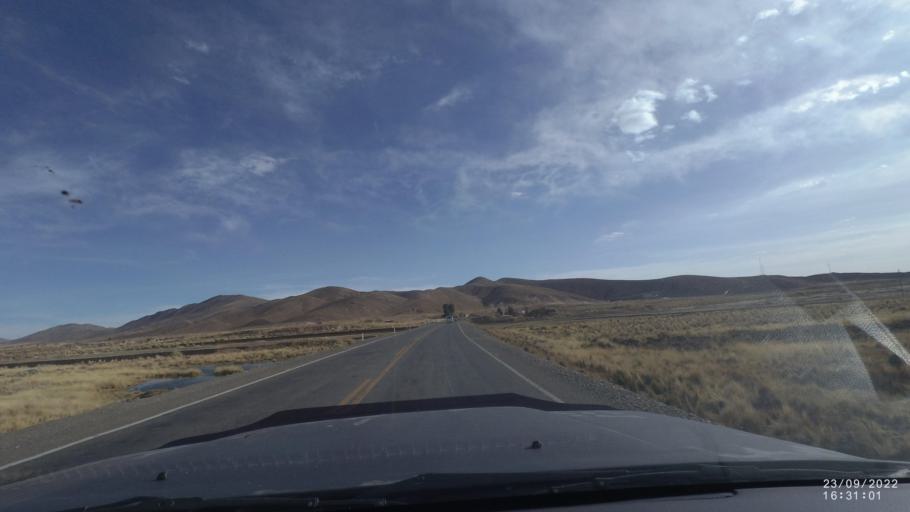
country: BO
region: Oruro
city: Machacamarca
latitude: -18.1621
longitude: -66.9874
